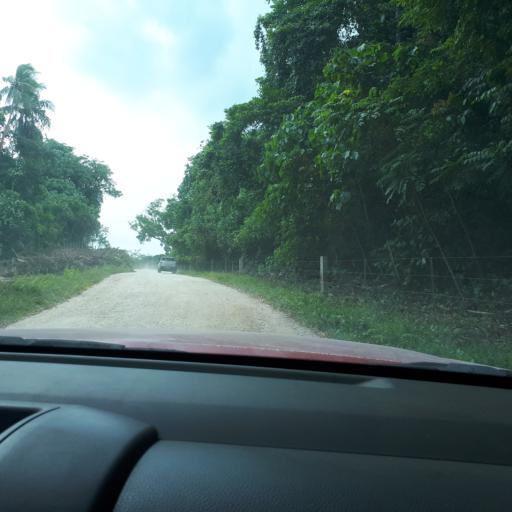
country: VU
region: Sanma
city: Luganville
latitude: -15.5778
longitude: 167.0312
